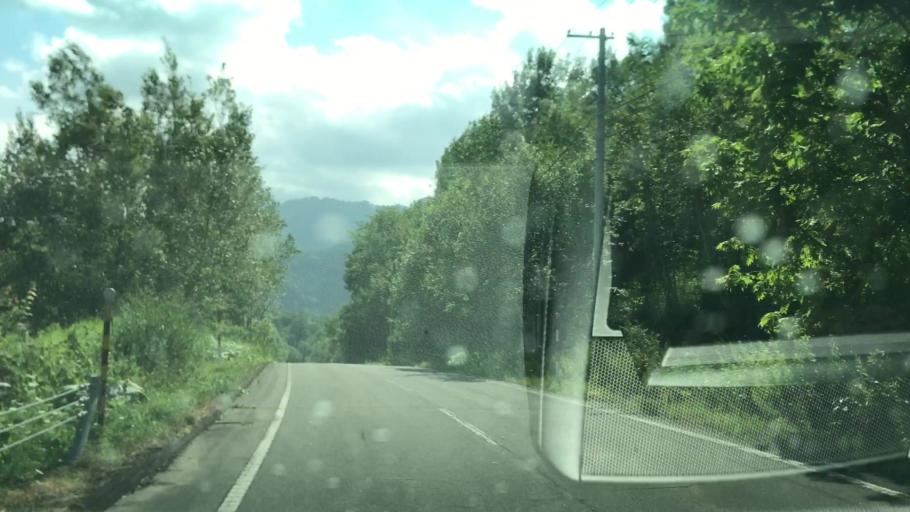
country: JP
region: Hokkaido
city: Shimo-furano
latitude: 42.8506
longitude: 142.4317
